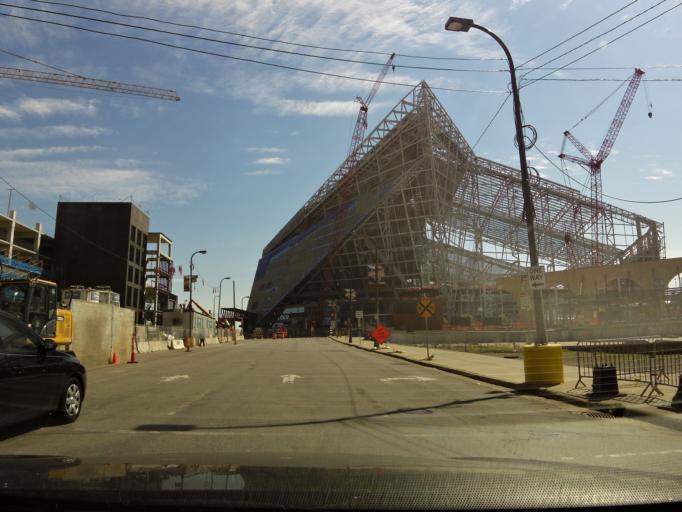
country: US
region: Minnesota
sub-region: Hennepin County
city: Minneapolis
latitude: 44.9757
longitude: -93.2603
